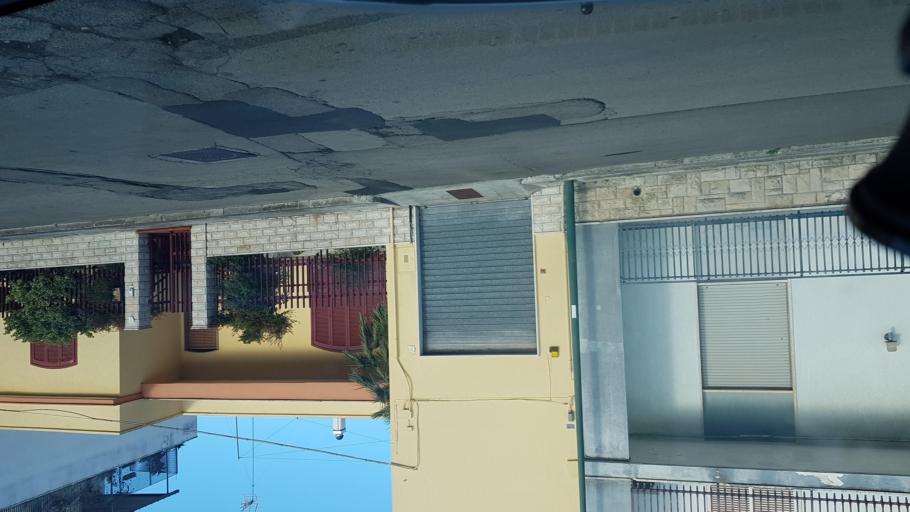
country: IT
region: Apulia
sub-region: Provincia di Lecce
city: Guagnano
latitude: 40.3991
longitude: 17.9478
